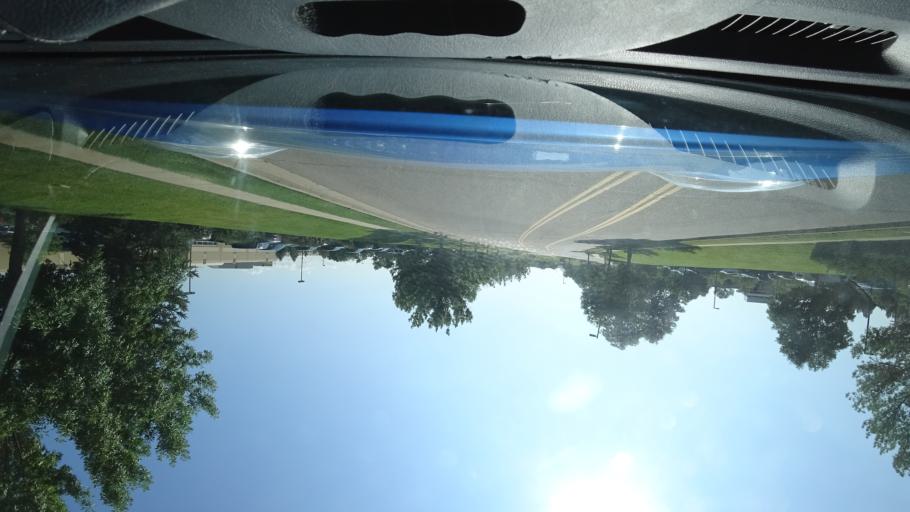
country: US
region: Colorado
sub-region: Adams County
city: Aurora
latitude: 39.7171
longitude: -104.7980
